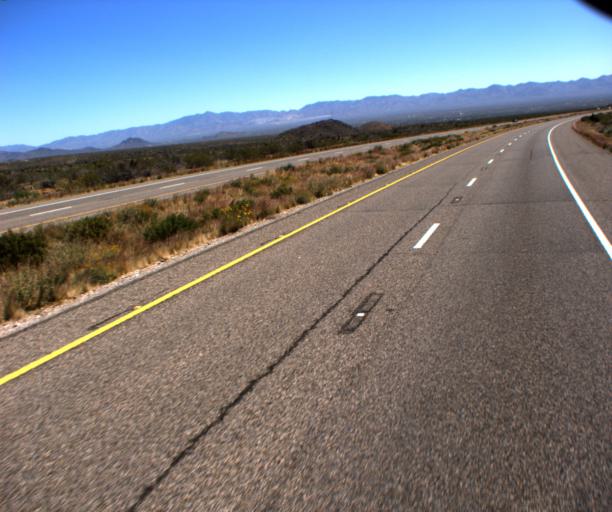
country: US
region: Arizona
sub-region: Mohave County
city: Golden Valley
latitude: 35.2287
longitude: -114.3724
